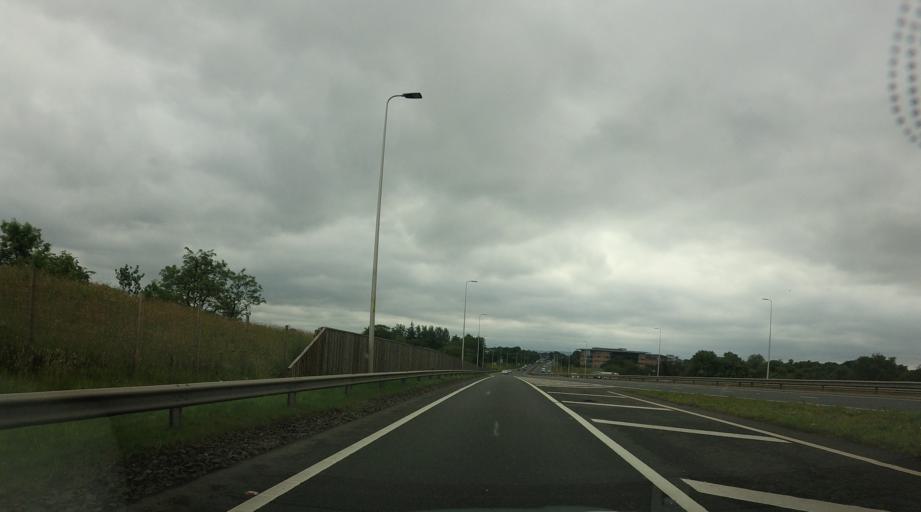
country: GB
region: Scotland
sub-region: North Lanarkshire
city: Bellshill
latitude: 55.8355
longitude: -4.0256
